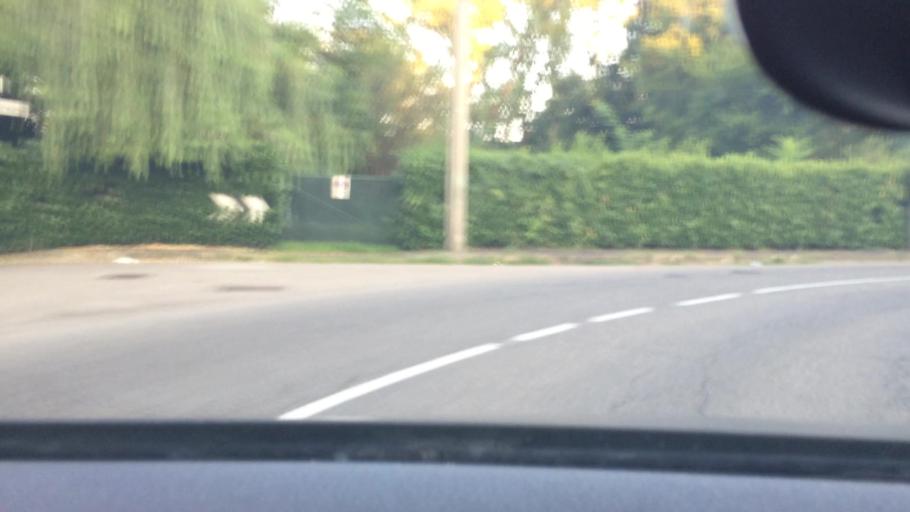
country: IT
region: Lombardy
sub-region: Provincia di Como
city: Rovello Porro
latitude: 45.6519
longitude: 9.0446
